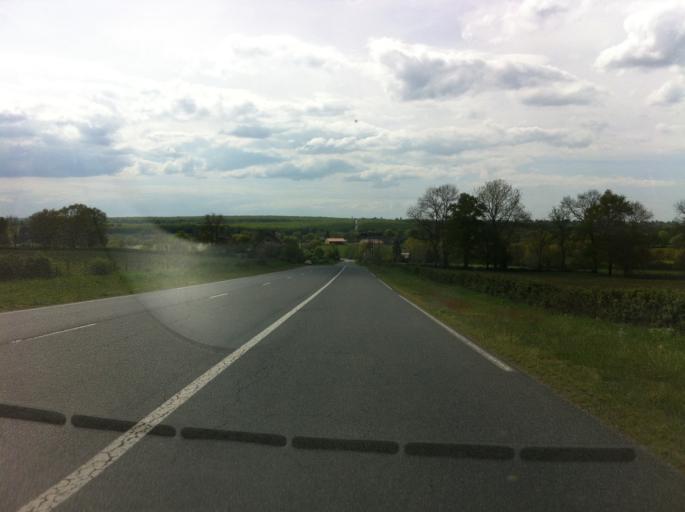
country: FR
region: Auvergne
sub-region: Departement de l'Allier
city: Chantelle
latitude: 46.3186
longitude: 3.1212
